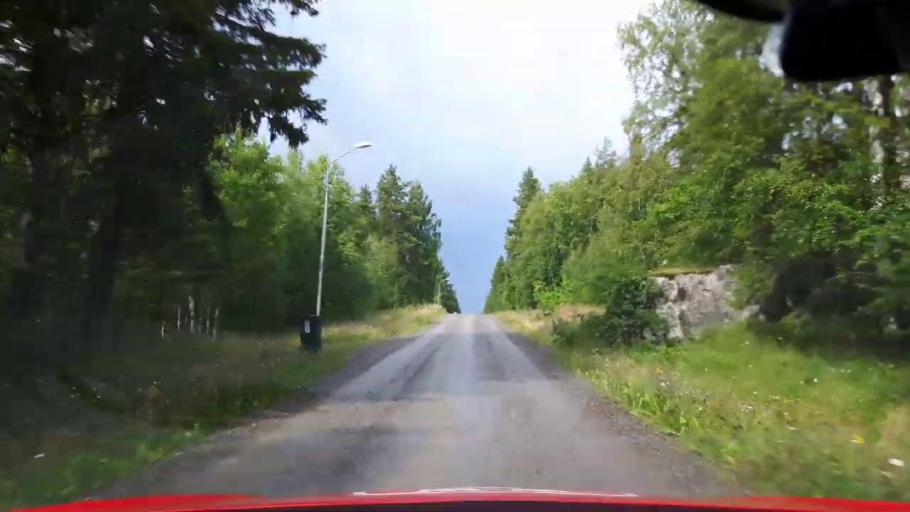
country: SE
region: Jaemtland
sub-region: Stroemsunds Kommun
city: Stroemsund
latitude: 64.0625
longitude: 15.8896
